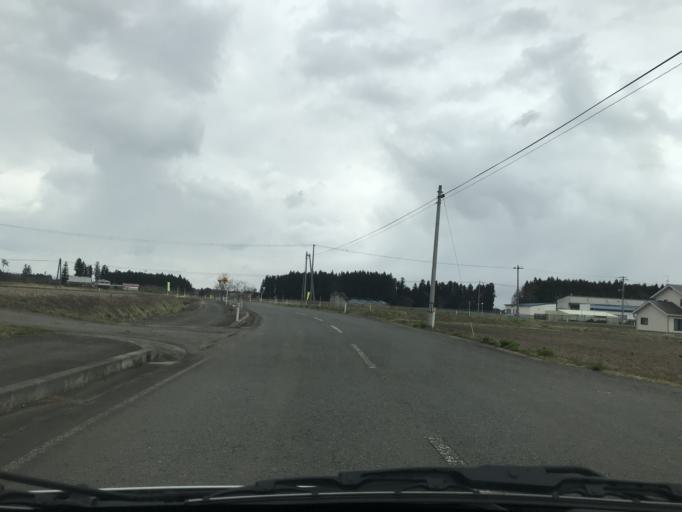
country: JP
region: Iwate
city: Mizusawa
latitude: 39.0850
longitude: 141.0800
